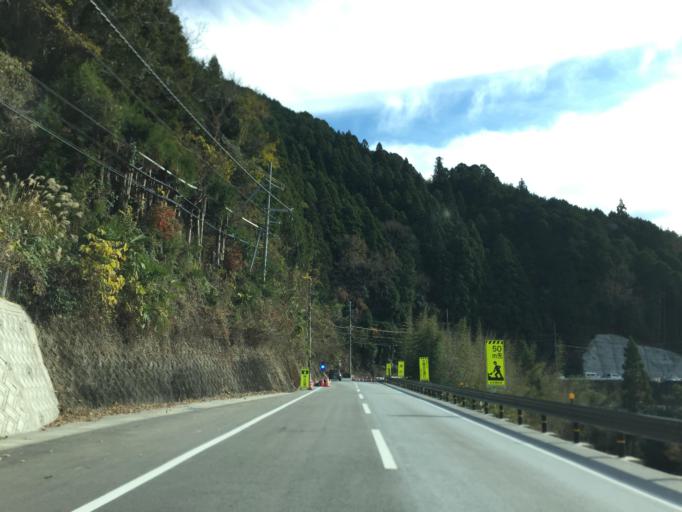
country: JP
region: Wakayama
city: Iwade
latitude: 34.1409
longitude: 135.3862
